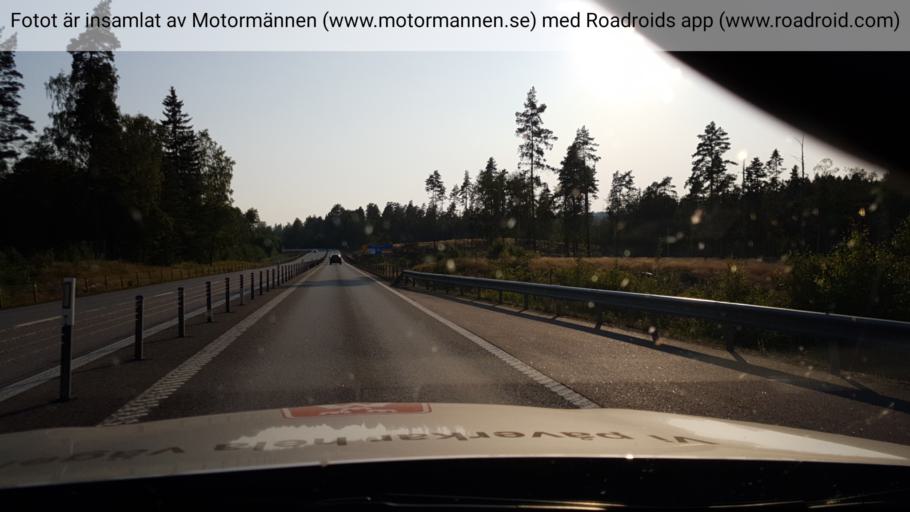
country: SE
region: OErebro
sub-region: Laxa Kommun
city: Laxa
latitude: 58.9748
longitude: 14.5526
